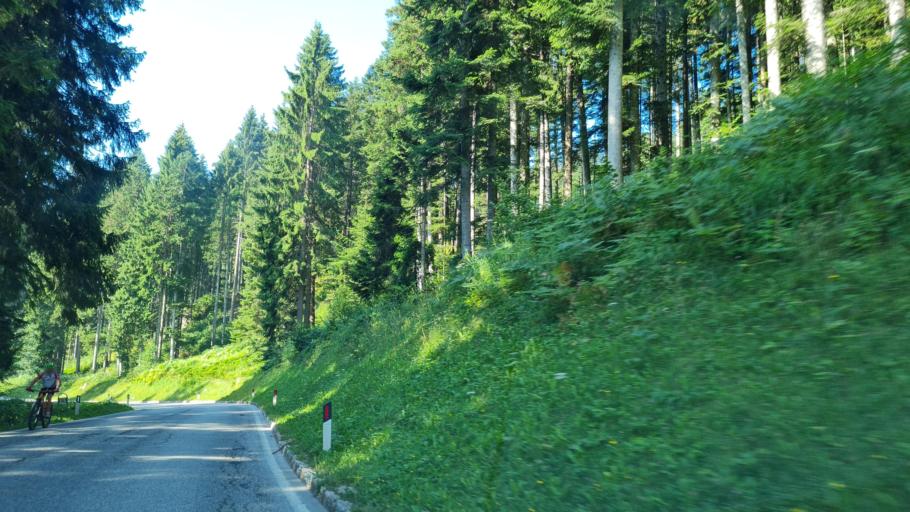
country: IT
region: Trentino-Alto Adige
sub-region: Provincia di Trento
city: Gionghi-Cappella
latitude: 45.9615
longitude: 11.2934
